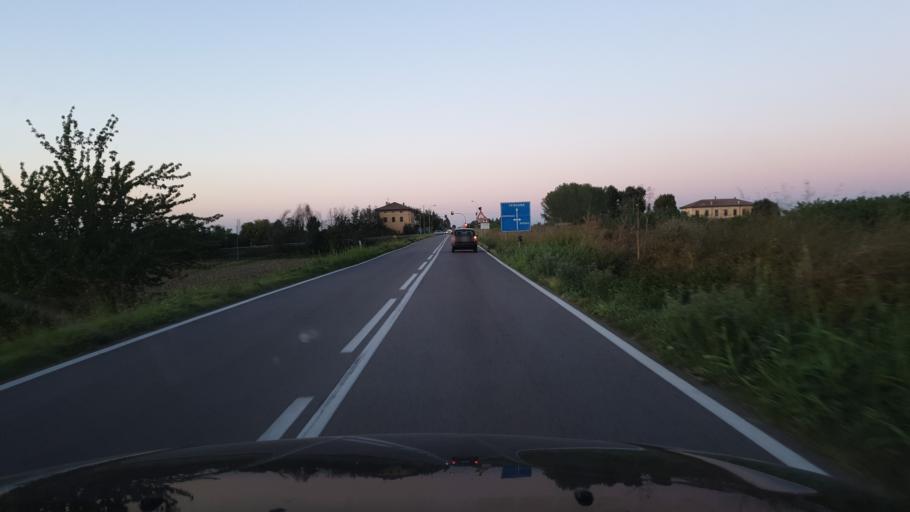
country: IT
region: Emilia-Romagna
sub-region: Provincia di Bologna
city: Minerbio
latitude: 44.6375
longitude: 11.4707
